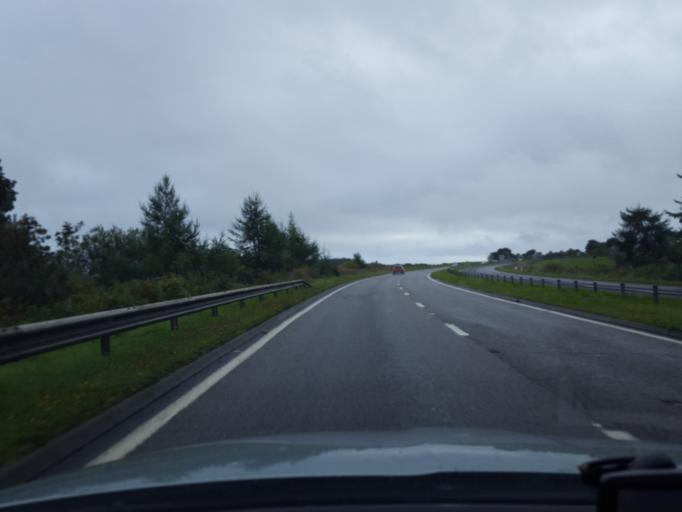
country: GB
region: Scotland
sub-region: Aberdeenshire
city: Stonehaven
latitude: 56.9508
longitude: -2.2306
